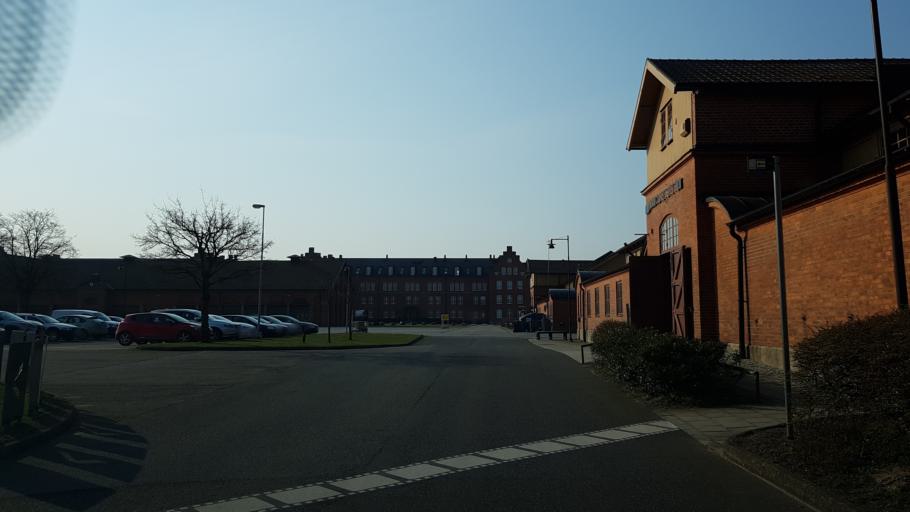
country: SE
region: Skane
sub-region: Ystads Kommun
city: Ystad
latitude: 55.4339
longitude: 13.8437
